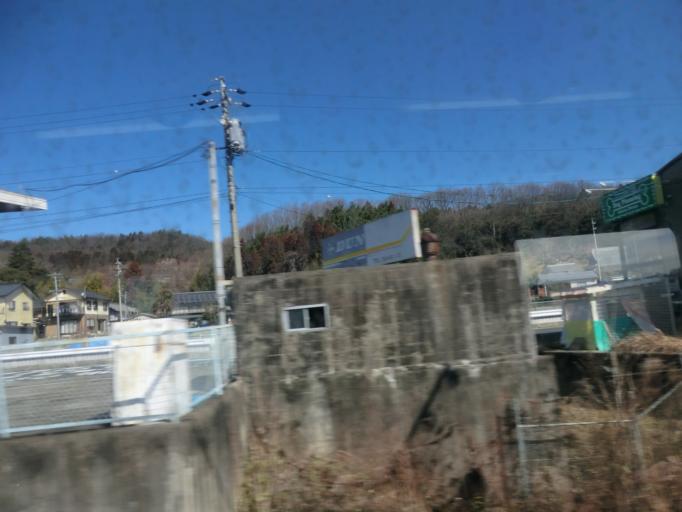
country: JP
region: Gifu
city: Toki
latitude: 35.3664
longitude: 137.2113
